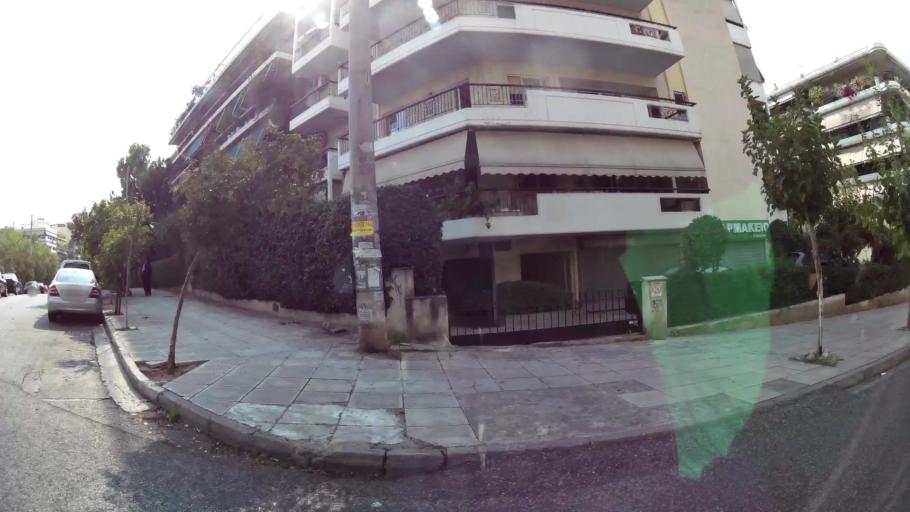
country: GR
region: Attica
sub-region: Nomarchia Athinas
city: Galatsi
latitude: 38.0223
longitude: 23.7414
